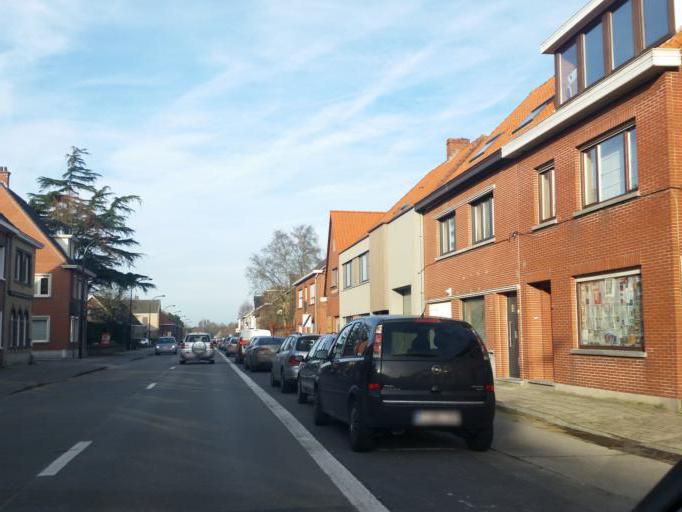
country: BE
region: Flanders
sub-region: Provincie Oost-Vlaanderen
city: Knesselare
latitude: 51.1414
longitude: 3.4096
